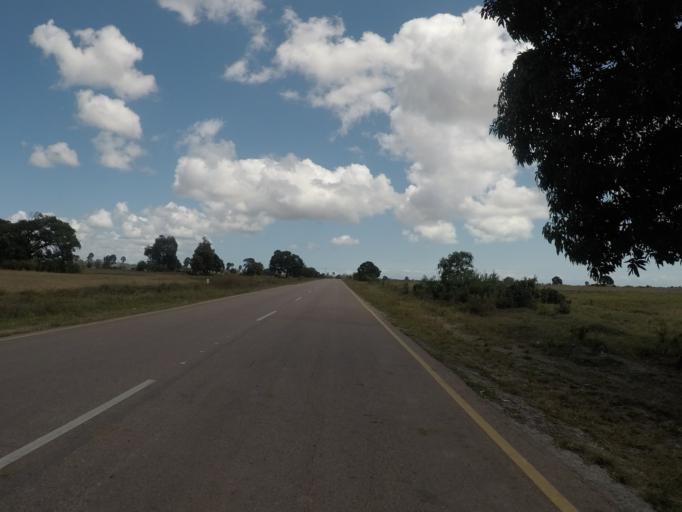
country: TZ
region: Zanzibar Central/South
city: Koani
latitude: -6.1946
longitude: 39.3704
